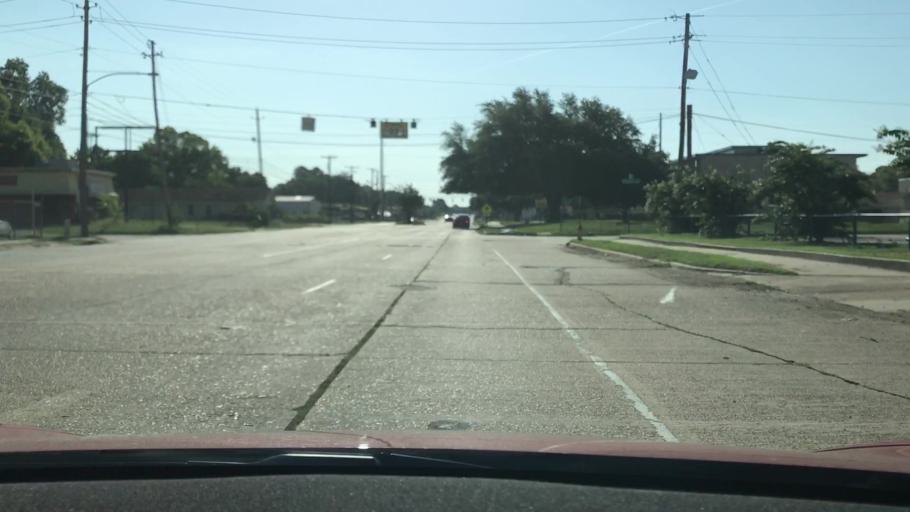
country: US
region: Louisiana
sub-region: Bossier Parish
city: Bossier City
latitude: 32.4420
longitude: -93.7657
